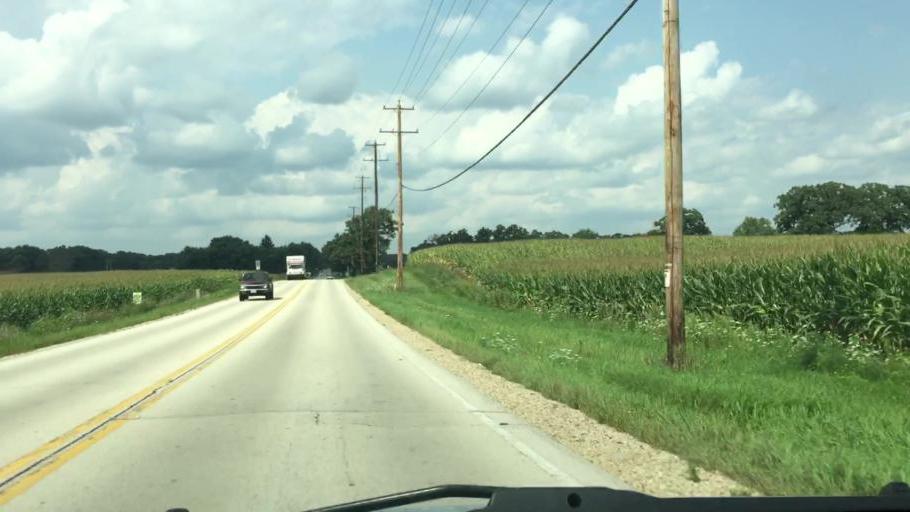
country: US
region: Wisconsin
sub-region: Waukesha County
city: North Prairie
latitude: 42.9407
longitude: -88.4055
